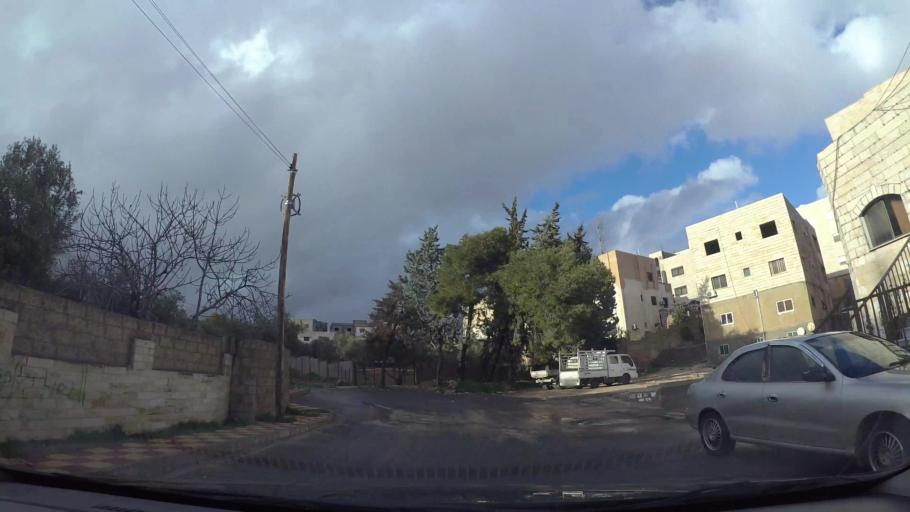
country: JO
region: Amman
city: Amman
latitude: 32.0034
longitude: 35.9217
